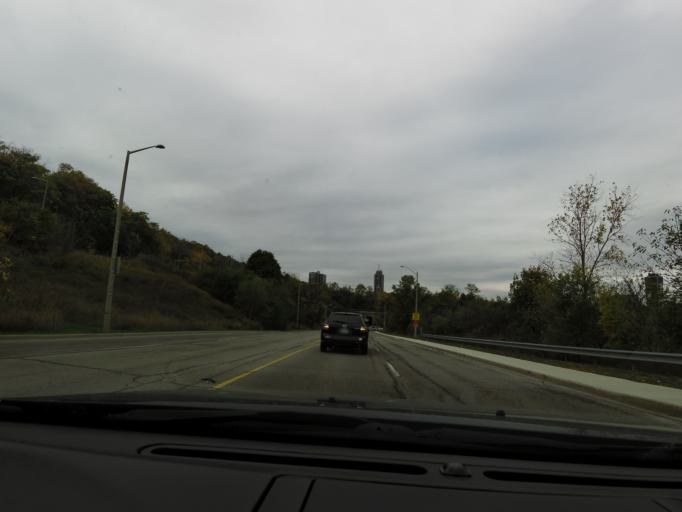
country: CA
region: Ontario
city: Hamilton
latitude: 43.2465
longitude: -79.8572
